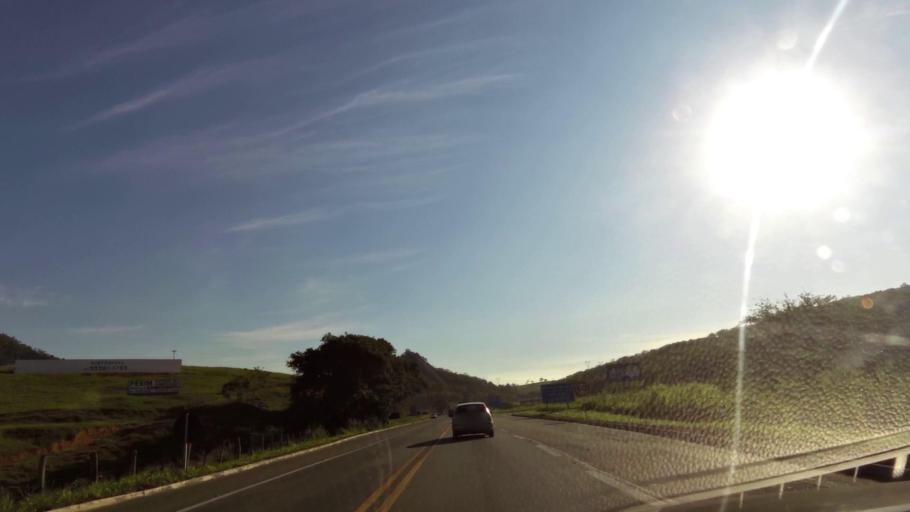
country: BR
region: Espirito Santo
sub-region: Guarapari
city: Guarapari
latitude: -20.5248
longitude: -40.4800
